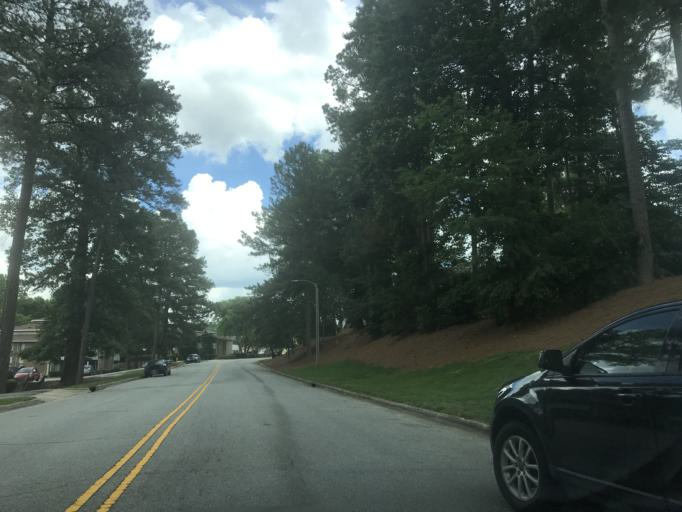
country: US
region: North Carolina
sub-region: Wake County
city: Raleigh
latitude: 35.8365
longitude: -78.6177
